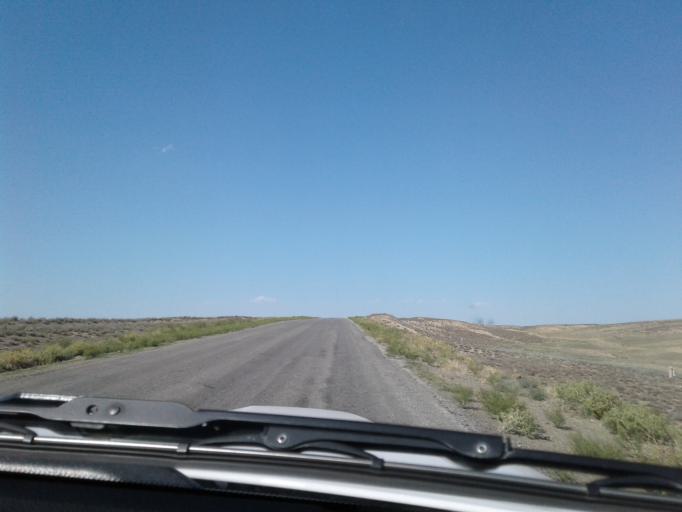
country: TM
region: Balkan
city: Magtymguly
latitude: 38.6349
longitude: 56.2467
